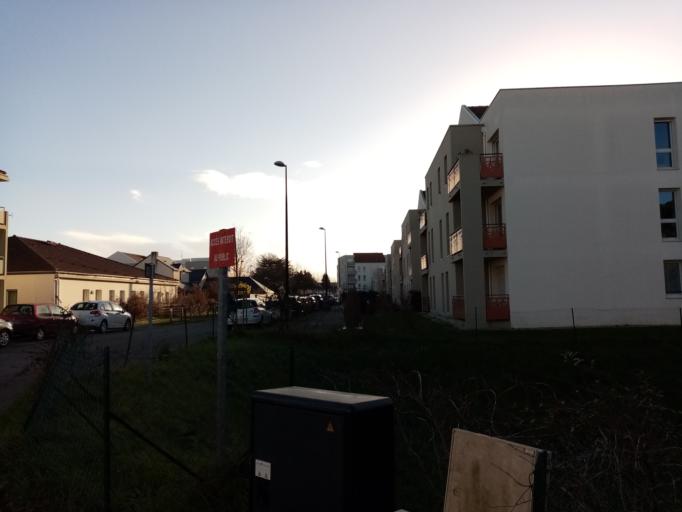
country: FR
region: Pays de la Loire
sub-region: Departement de la Loire-Atlantique
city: Saint-Sebastien-sur-Loire
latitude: 47.1904
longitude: -1.5022
